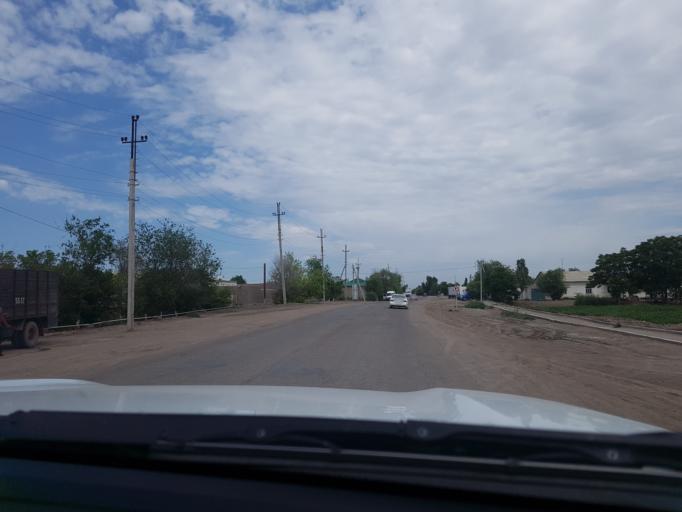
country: TM
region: Dasoguz
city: Koeneuergench
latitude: 42.3130
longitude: 59.1382
